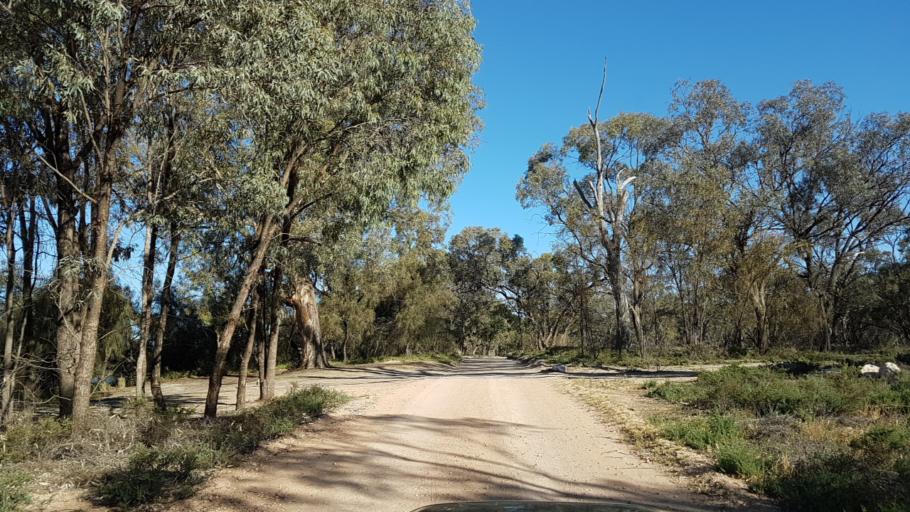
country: AU
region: South Australia
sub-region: Loxton Waikerie
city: Waikerie
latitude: -34.1610
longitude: 140.0313
